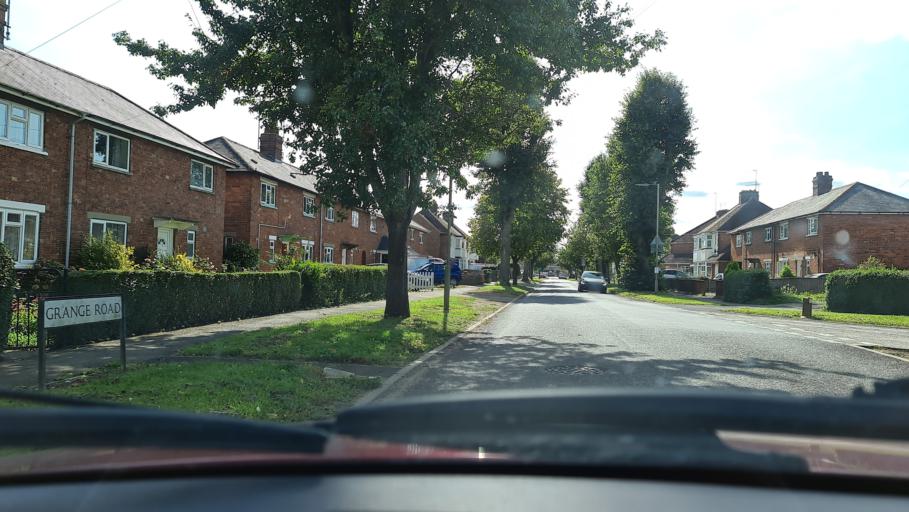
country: GB
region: England
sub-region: Oxfordshire
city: Banbury
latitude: 52.0482
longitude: -1.3369
